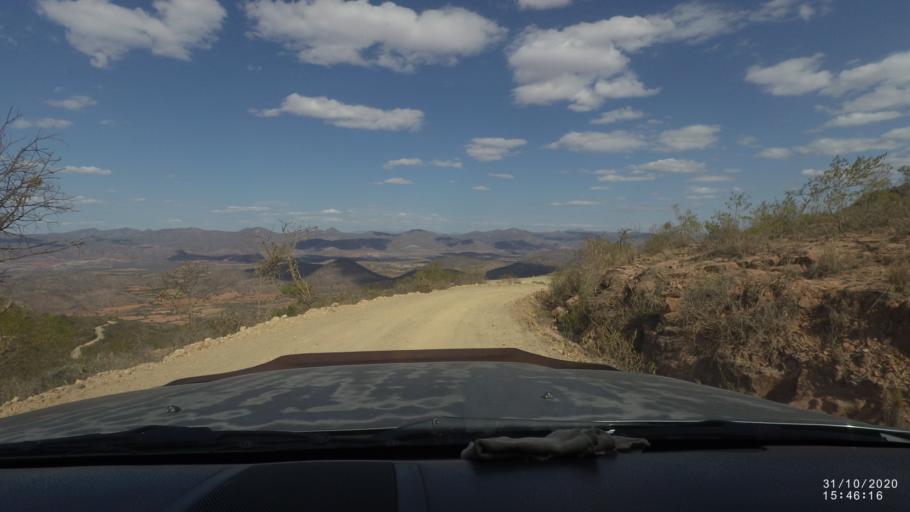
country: BO
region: Chuquisaca
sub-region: Provincia Zudanez
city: Mojocoya
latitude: -18.3159
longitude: -64.7169
